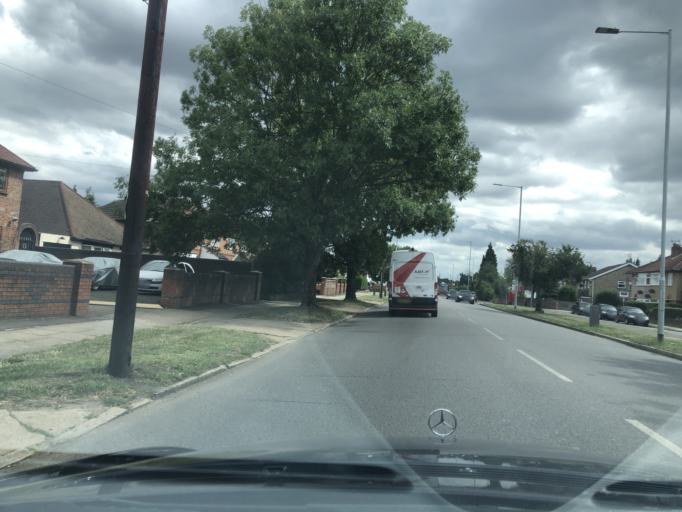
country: GB
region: England
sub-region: Greater London
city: Ruislip
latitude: 51.5515
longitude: -0.4019
